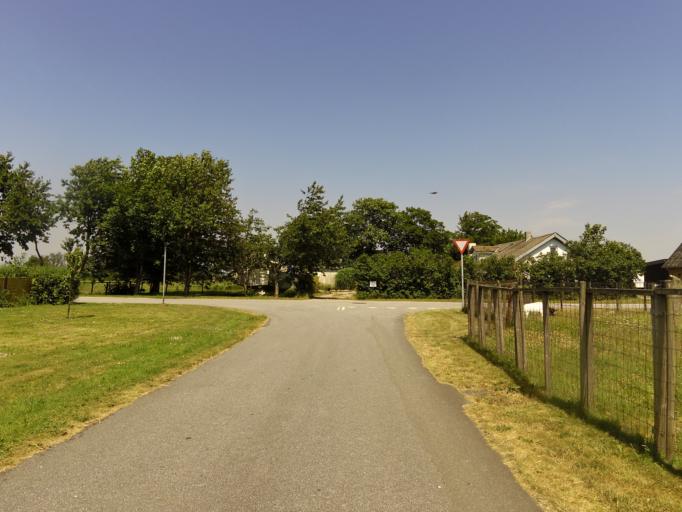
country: DK
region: South Denmark
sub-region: Haderslev Kommune
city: Vojens
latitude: 55.1580
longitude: 9.2554
